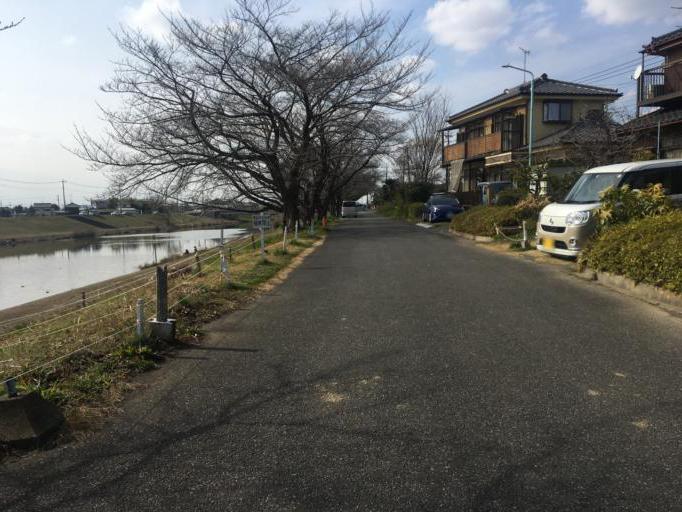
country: JP
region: Saitama
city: Kamifukuoka
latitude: 35.8823
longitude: 139.5560
